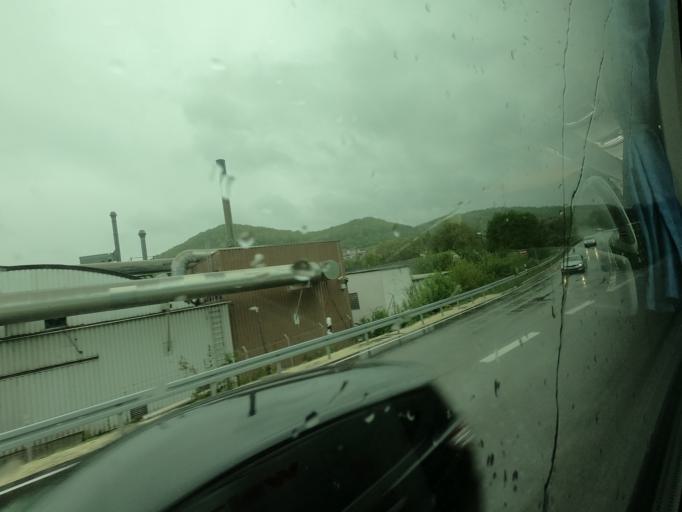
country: DE
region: Baden-Wuerttemberg
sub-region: Regierungsbezirk Stuttgart
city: Oberkochen
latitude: 48.8118
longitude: 10.1254
